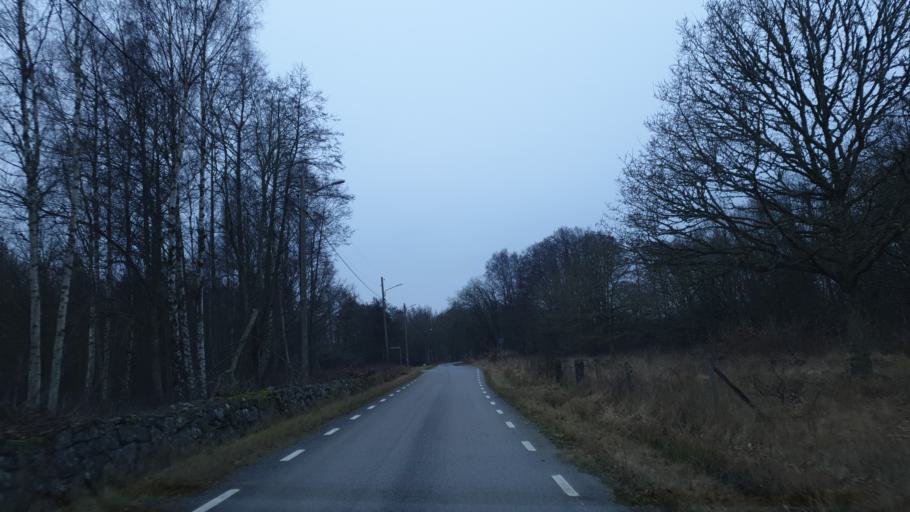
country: SE
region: Blekinge
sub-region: Karlskrona Kommun
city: Karlskrona
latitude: 56.1068
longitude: 15.6110
